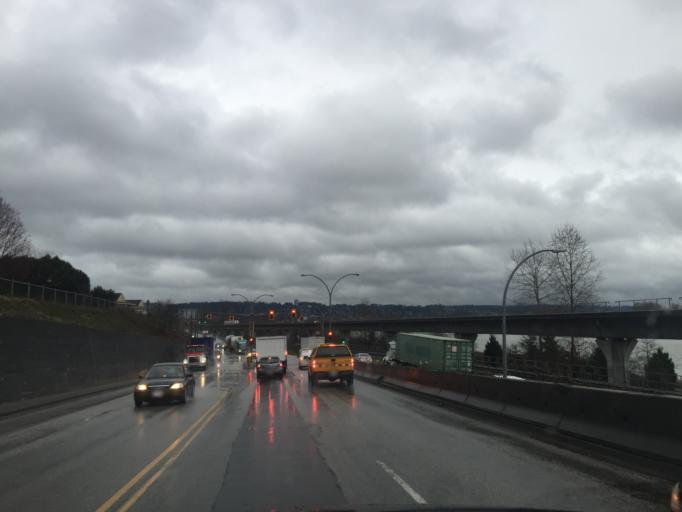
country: CA
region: British Columbia
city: New Westminster
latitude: 49.2136
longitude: -122.8952
